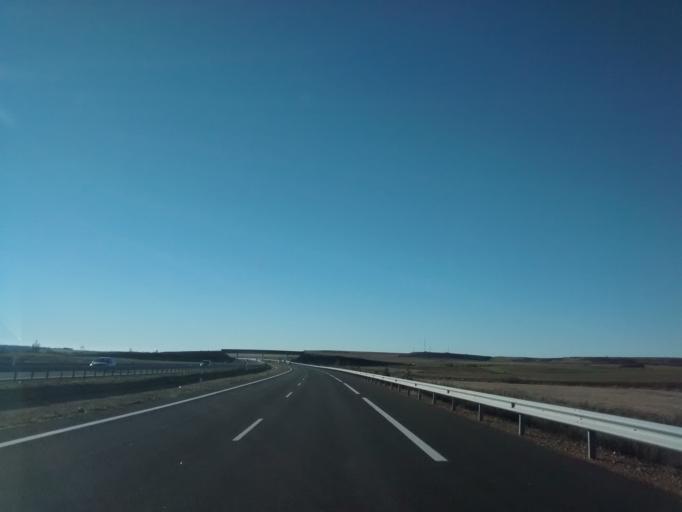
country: ES
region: Castille and Leon
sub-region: Provincia de Palencia
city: Espinosa de Villagonzalo
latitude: 42.4890
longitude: -4.3850
